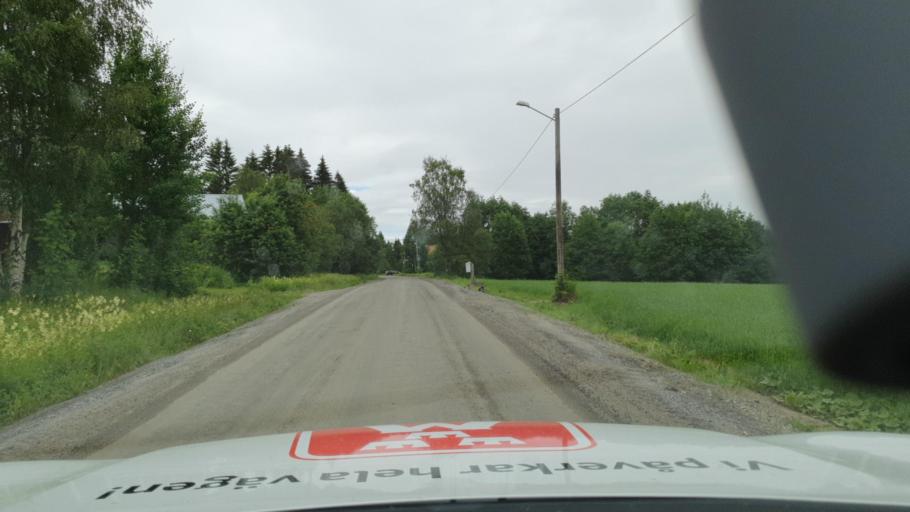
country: SE
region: Vaesterbotten
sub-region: Nordmalings Kommun
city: Nordmaling
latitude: 63.6476
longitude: 19.4318
